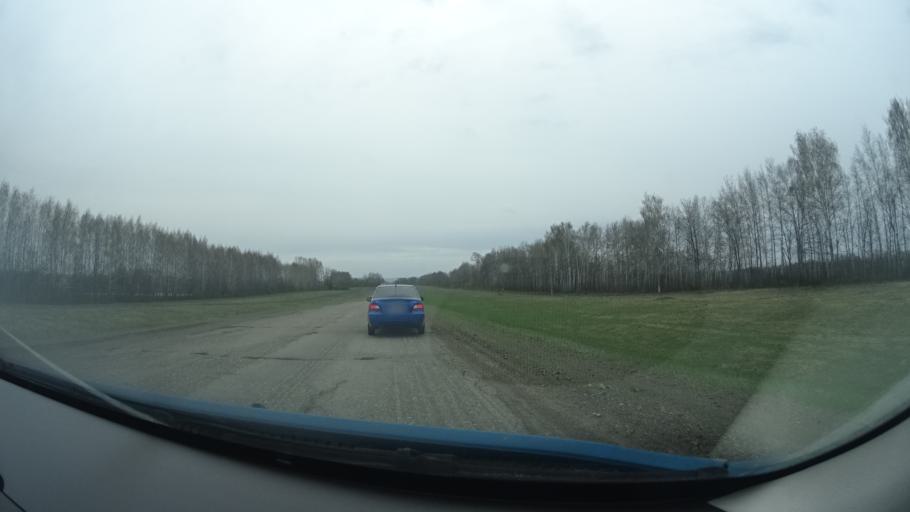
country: RU
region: Bashkortostan
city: Birsk
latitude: 55.2672
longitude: 55.7316
